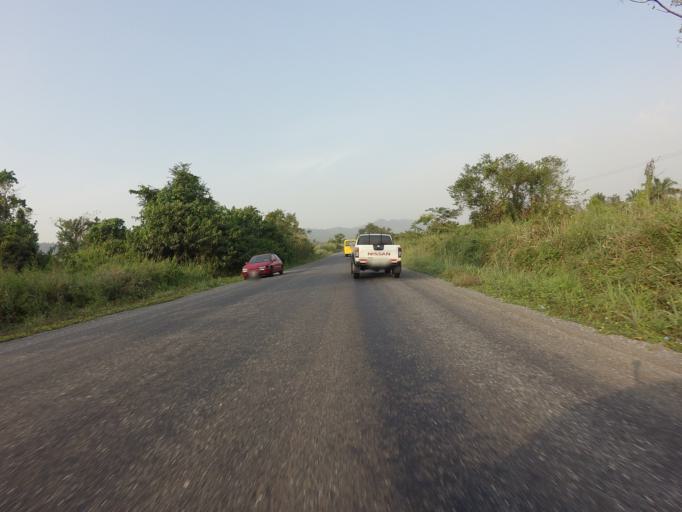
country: GH
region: Volta
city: Ho
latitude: 6.4759
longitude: 0.2298
